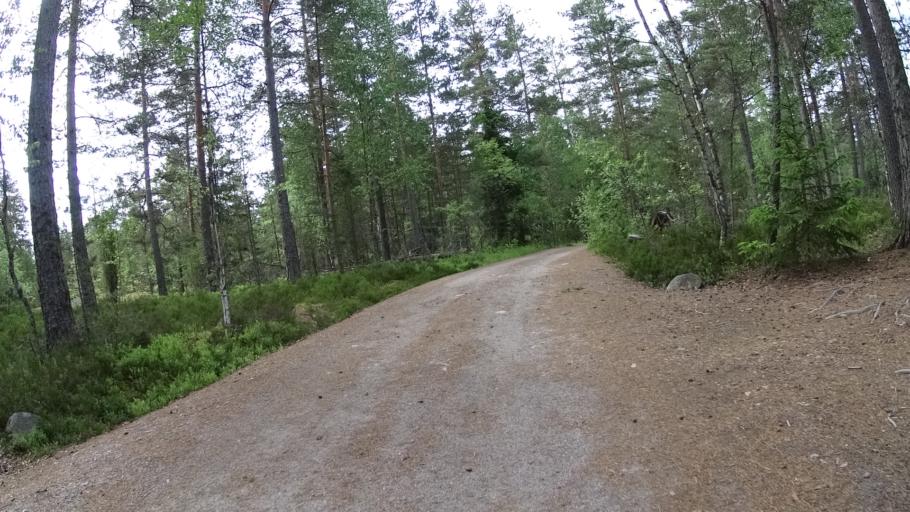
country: FI
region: Uusimaa
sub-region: Helsinki
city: Espoo
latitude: 60.2911
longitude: 24.5234
